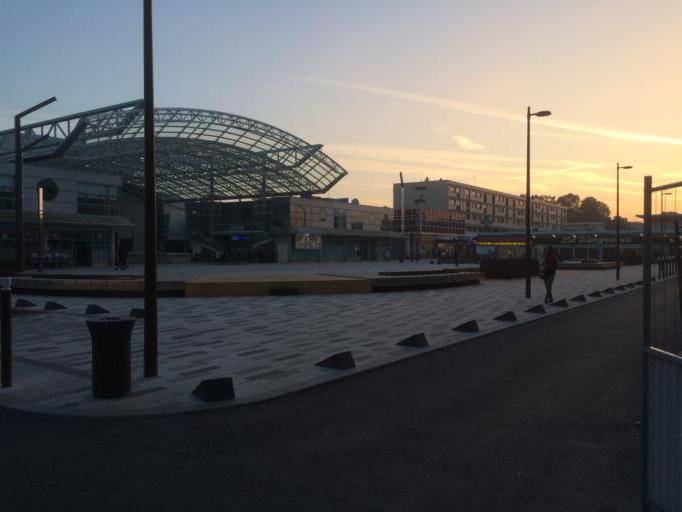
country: FR
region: Ile-de-France
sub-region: Departement de l'Essonne
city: Massy
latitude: 48.7327
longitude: 2.2897
